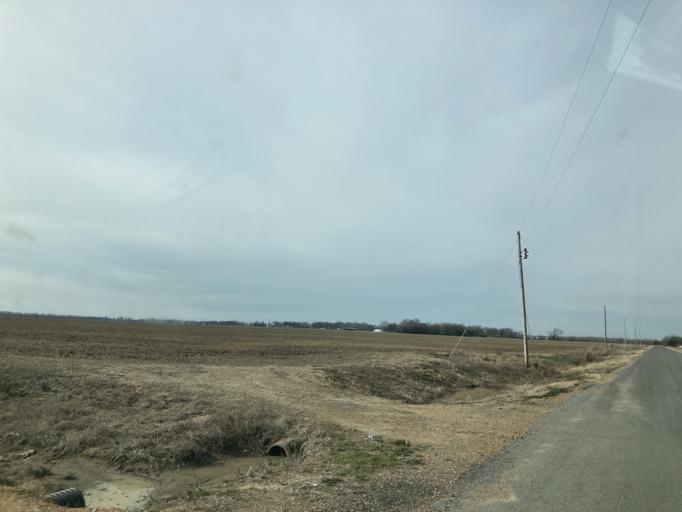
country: US
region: Mississippi
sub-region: Humphreys County
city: Belzoni
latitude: 33.0564
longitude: -90.6576
